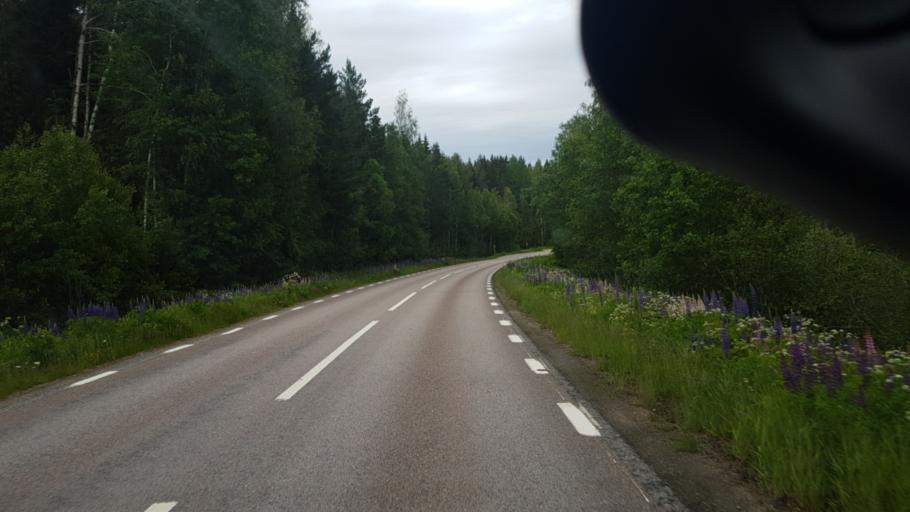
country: SE
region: Vaermland
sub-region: Eda Kommun
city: Amotfors
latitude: 59.7267
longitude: 12.2705
